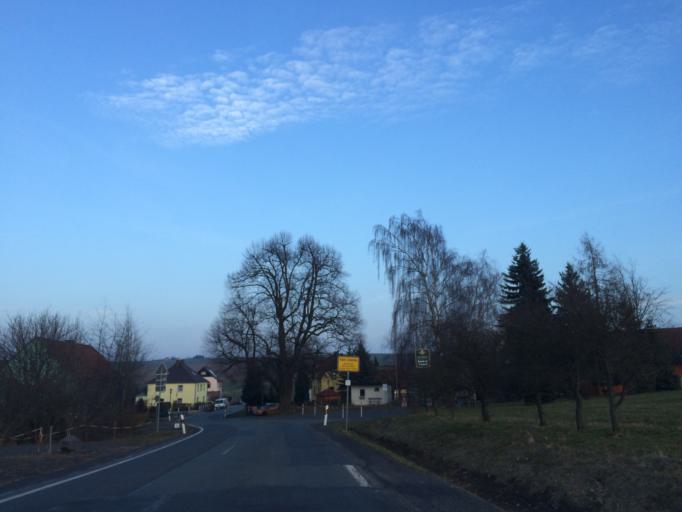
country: DE
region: Thuringia
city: Seisla
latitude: 50.6370
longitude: 11.5214
